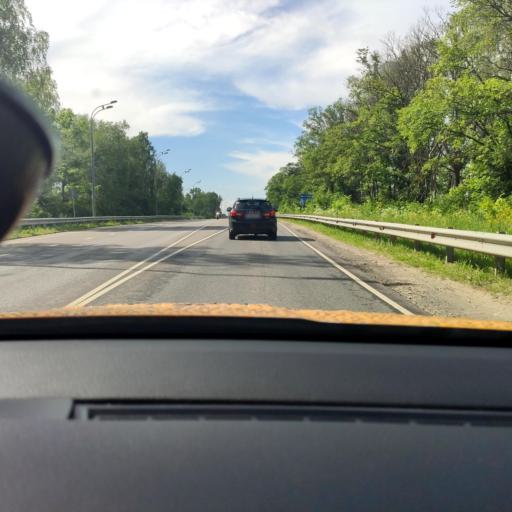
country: RU
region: Moskovskaya
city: Stupino
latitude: 54.9403
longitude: 38.0356
